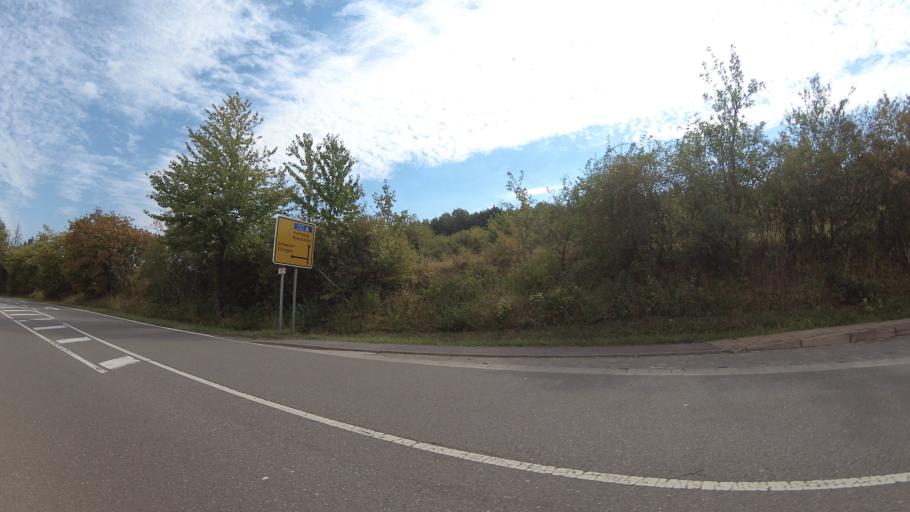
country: DE
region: Saarland
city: Gersheim
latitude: 49.1663
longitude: 7.2263
